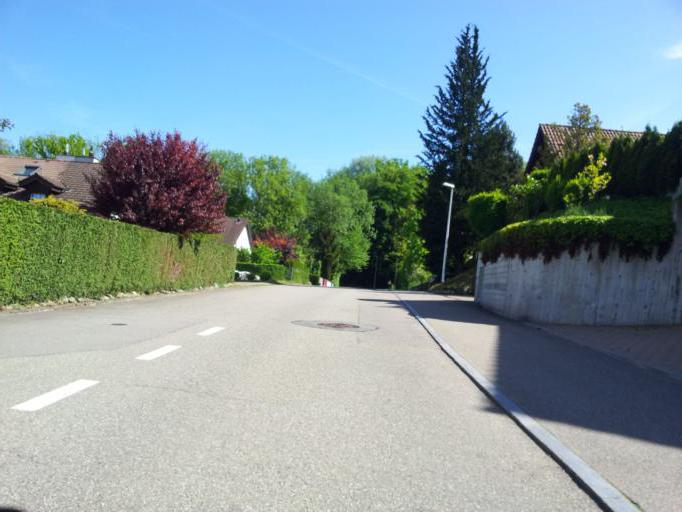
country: CH
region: Zurich
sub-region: Bezirk Dietikon
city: Dietikon / Oberdorf
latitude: 47.3950
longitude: 8.3814
